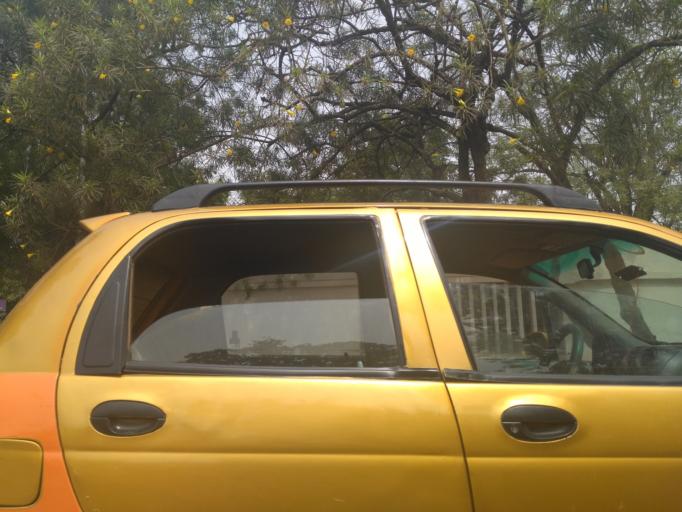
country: GH
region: Ashanti
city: Kumasi
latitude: 6.6762
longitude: -1.6207
